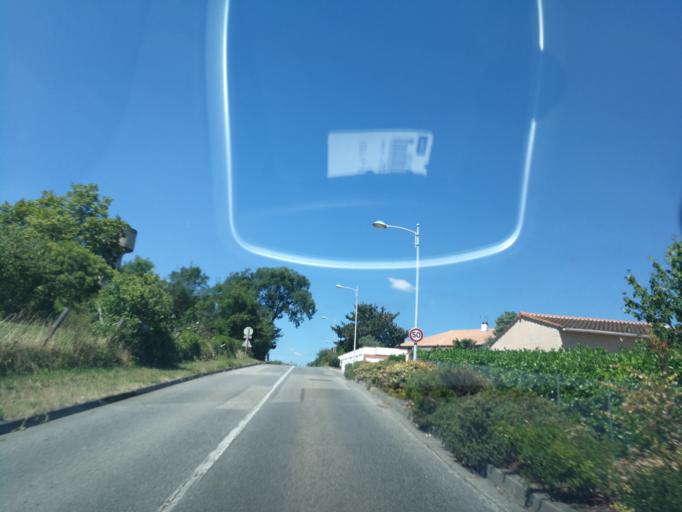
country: FR
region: Midi-Pyrenees
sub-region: Departement de la Haute-Garonne
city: Balma
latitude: 43.6178
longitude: 1.5054
